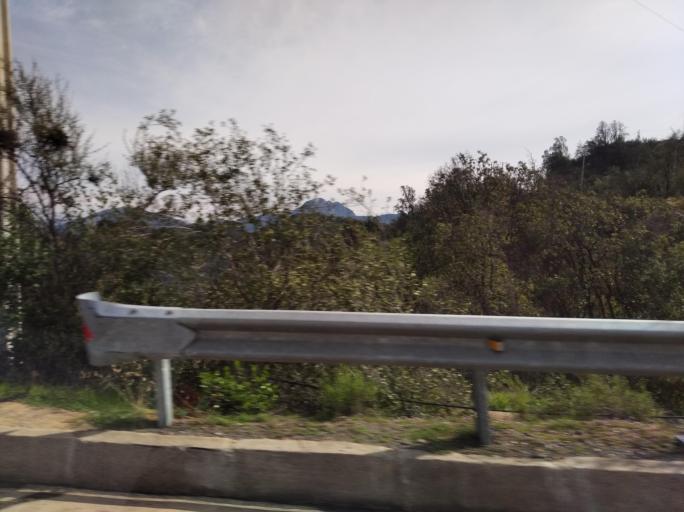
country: CL
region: Valparaiso
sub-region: Provincia de San Felipe
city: Llaillay
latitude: -33.0610
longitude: -71.0180
